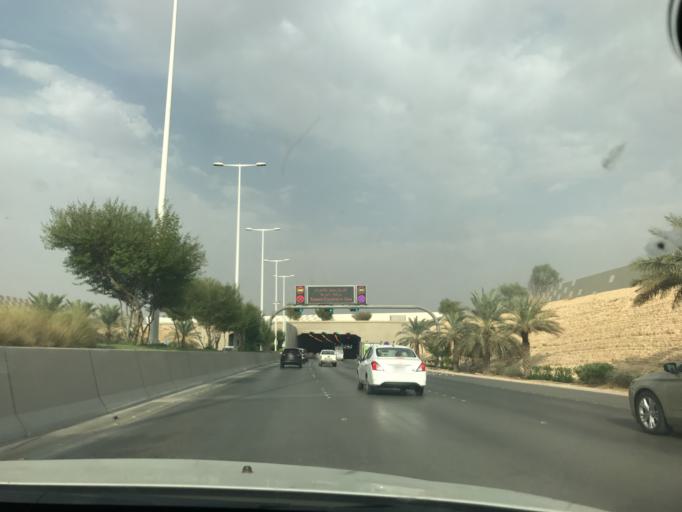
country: SA
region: Ar Riyad
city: Riyadh
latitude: 24.7311
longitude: 46.7248
